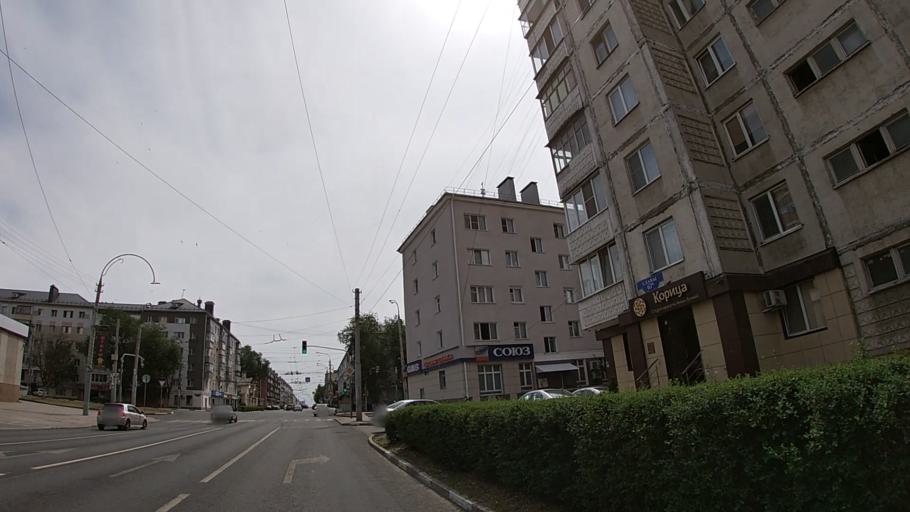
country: RU
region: Belgorod
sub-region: Belgorodskiy Rayon
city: Belgorod
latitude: 50.5988
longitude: 36.5792
